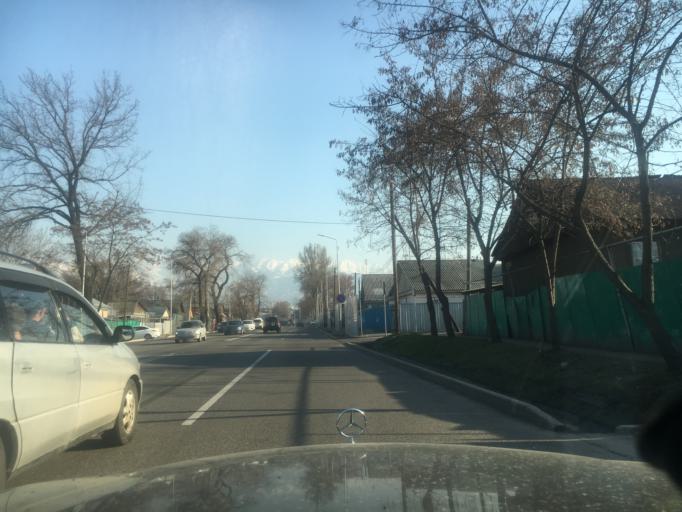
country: KZ
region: Almaty Qalasy
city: Almaty
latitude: 43.2818
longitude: 76.9392
